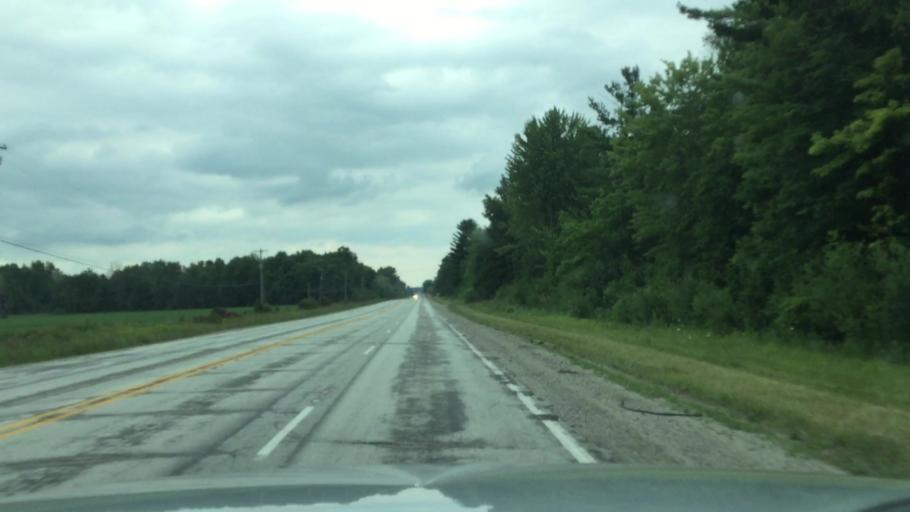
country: US
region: Michigan
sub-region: Saginaw County
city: Birch Run
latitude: 43.3117
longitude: -83.8158
